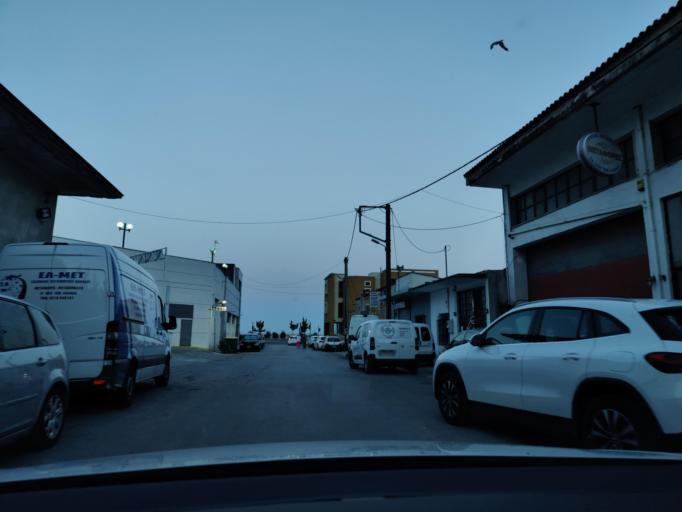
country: GR
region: East Macedonia and Thrace
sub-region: Nomos Kavalas
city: Kavala
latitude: 40.9292
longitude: 24.3899
